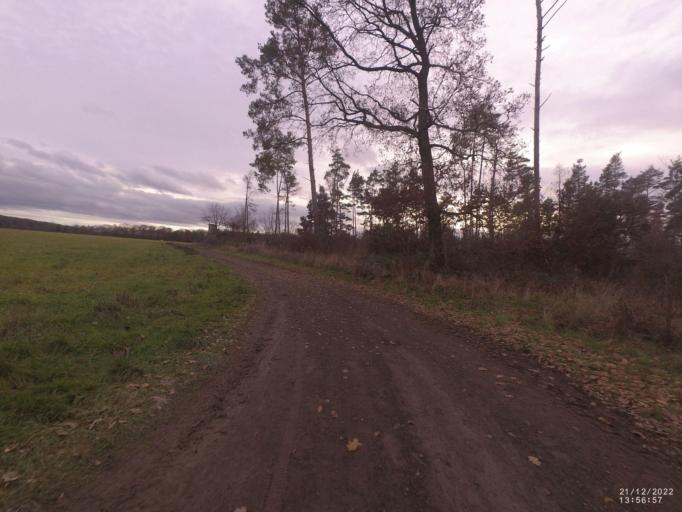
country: DE
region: Rheinland-Pfalz
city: Gonnersdorf
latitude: 50.5106
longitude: 7.2525
